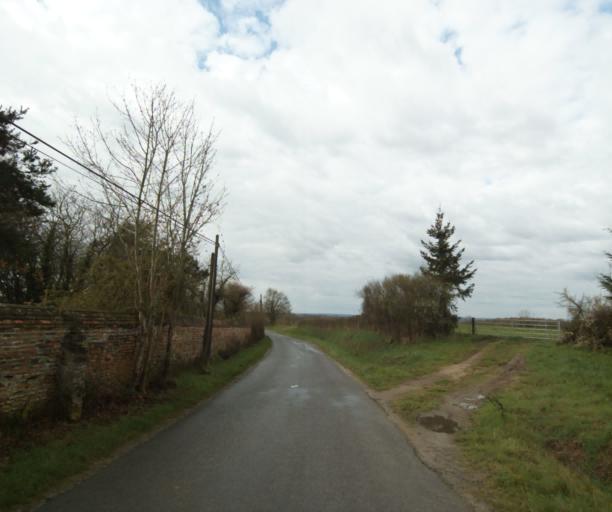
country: FR
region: Auvergne
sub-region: Departement de l'Allier
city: Toulon-sur-Allier
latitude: 46.5240
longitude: 3.3978
